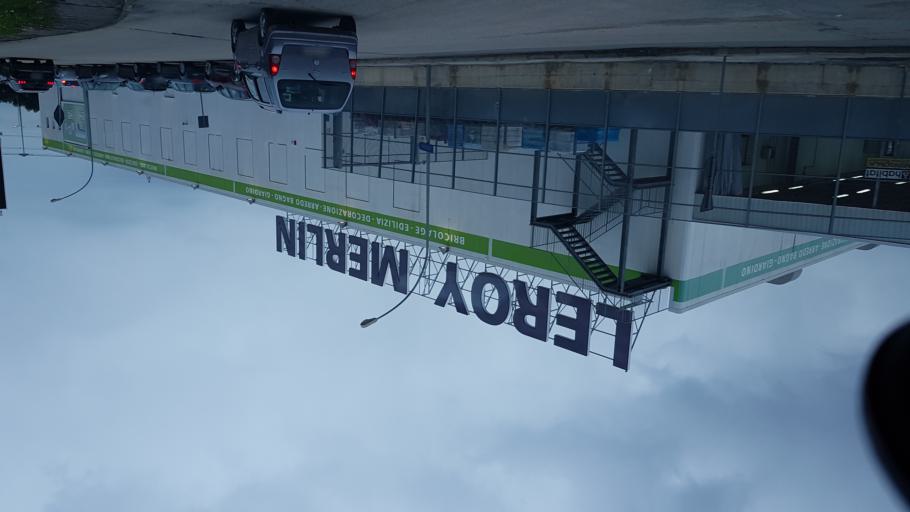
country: IT
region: Apulia
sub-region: Provincia di Brindisi
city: Mesagne
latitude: 40.5773
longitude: 17.8343
